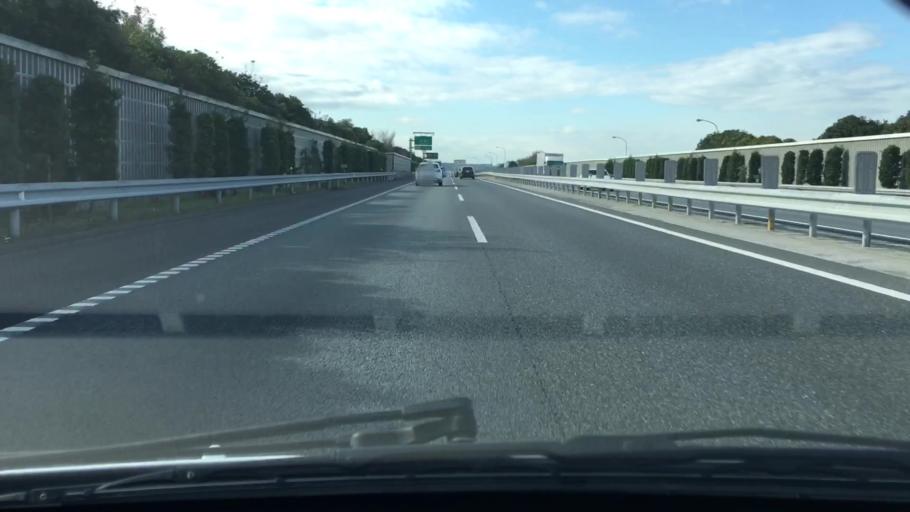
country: JP
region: Chiba
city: Ichihara
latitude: 35.5004
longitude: 140.0983
